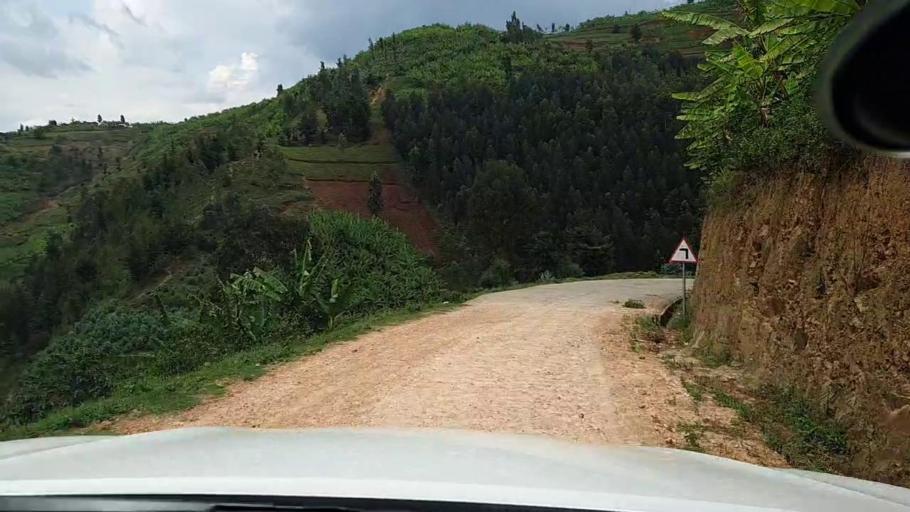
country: RW
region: Western Province
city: Kibuye
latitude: -2.1271
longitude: 29.4273
